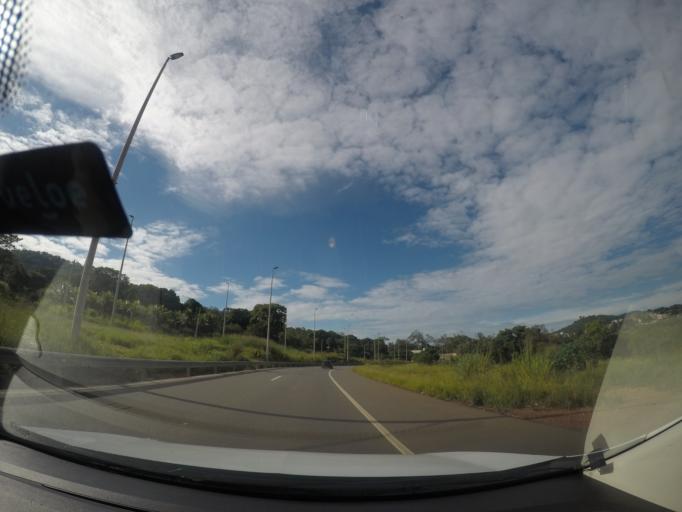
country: BR
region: Goias
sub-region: Goiania
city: Goiania
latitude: -16.6787
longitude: -49.1954
